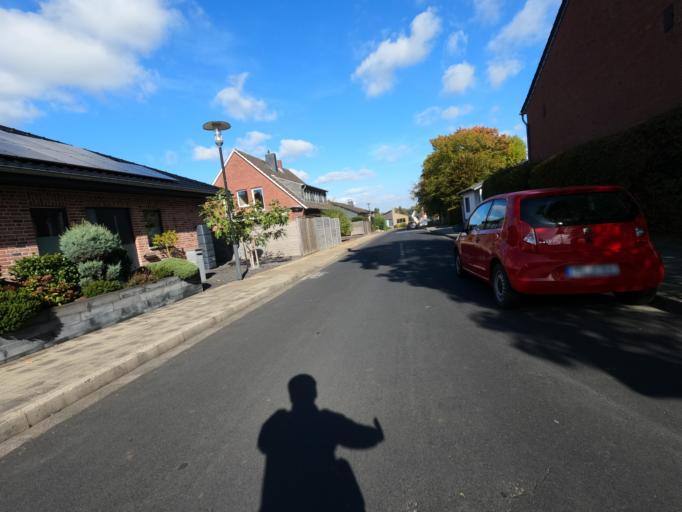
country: DE
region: North Rhine-Westphalia
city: Geilenkirchen
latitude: 50.9640
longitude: 6.1150
